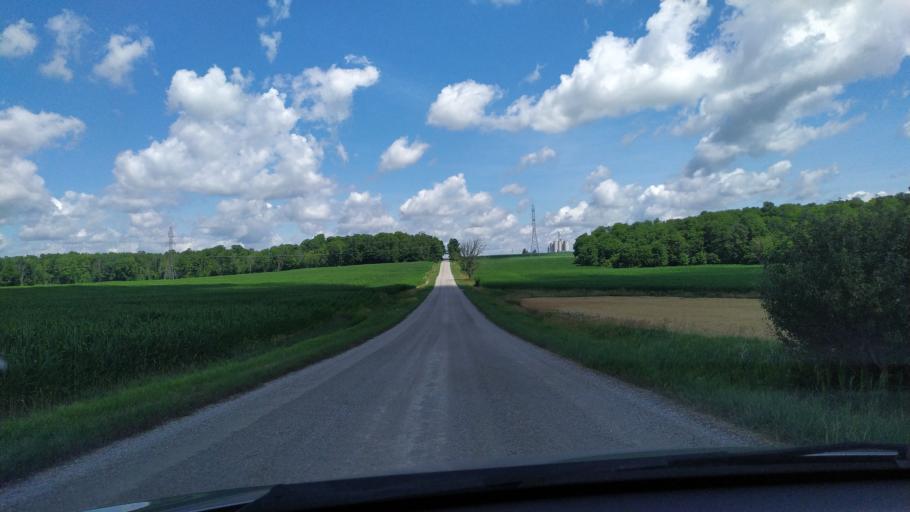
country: CA
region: Ontario
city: Stratford
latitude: 43.3736
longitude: -80.7616
